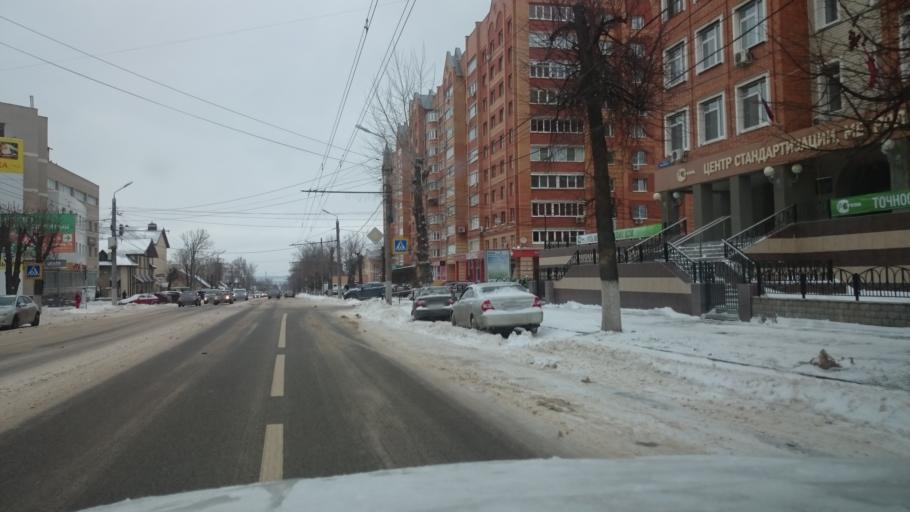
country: RU
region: Tula
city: Mendeleyevskiy
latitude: 54.1748
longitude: 37.5748
